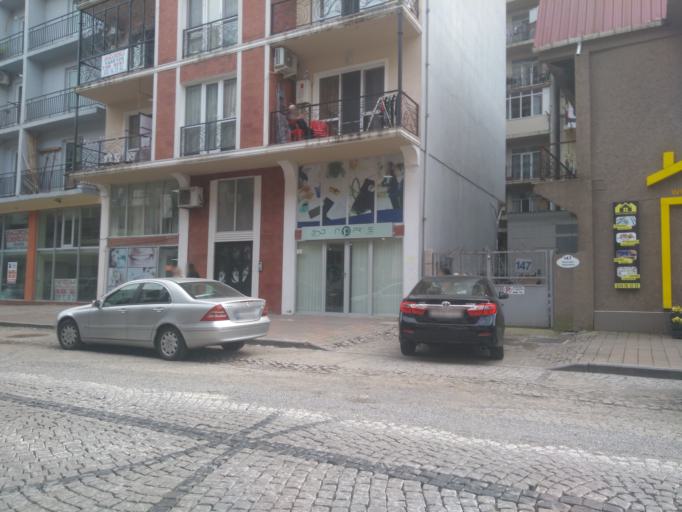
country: GE
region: Ajaria
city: Batumi
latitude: 41.6435
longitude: 41.6240
